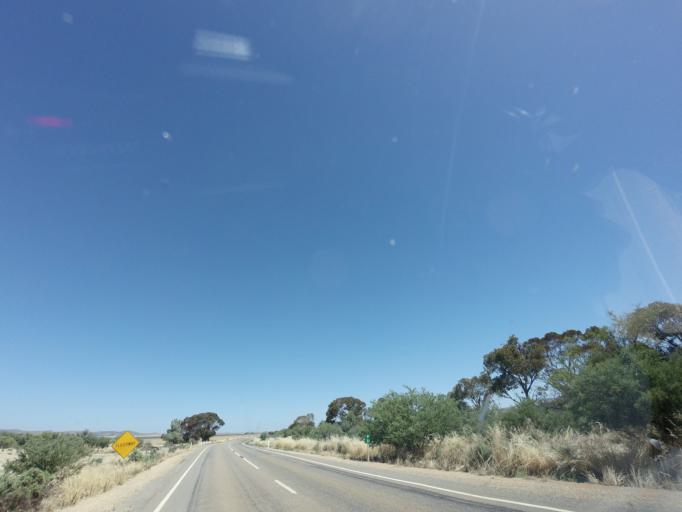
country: AU
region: South Australia
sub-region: Peterborough
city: Peterborough
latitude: -32.7628
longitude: 138.6546
